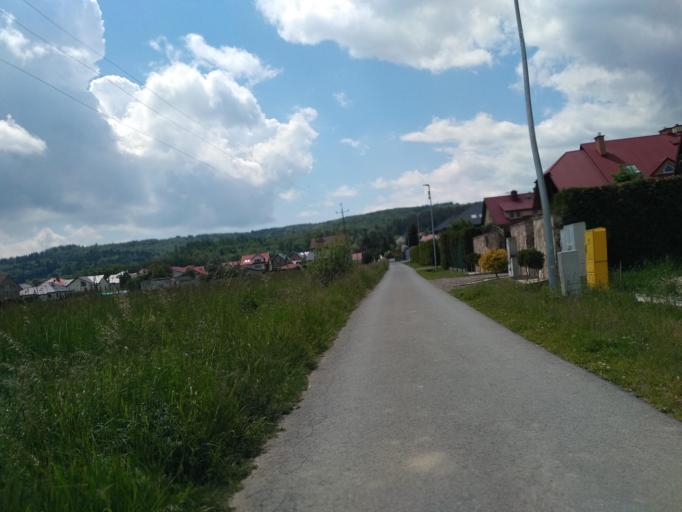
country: PL
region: Subcarpathian Voivodeship
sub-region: Powiat strzyzowski
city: Babica
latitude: 49.9306
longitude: 21.8533
